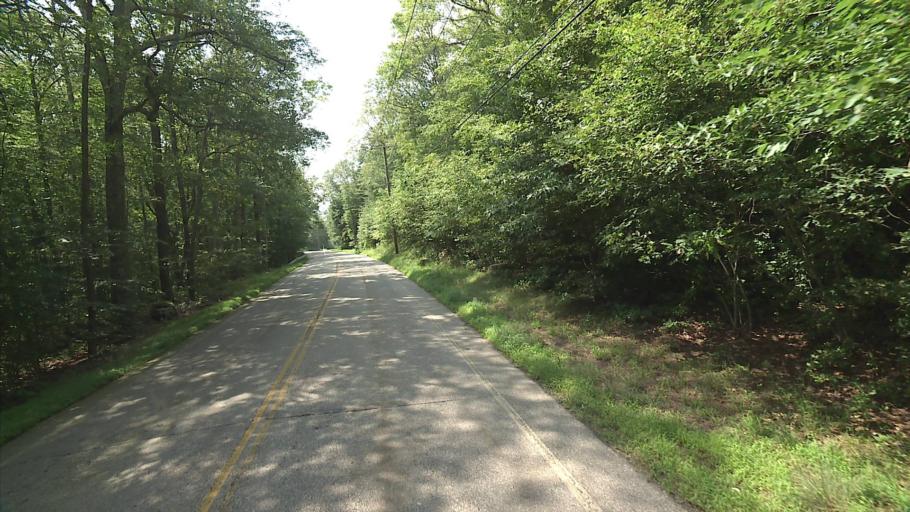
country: US
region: Connecticut
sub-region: Middlesex County
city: Essex Village
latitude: 41.4287
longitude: -72.3666
